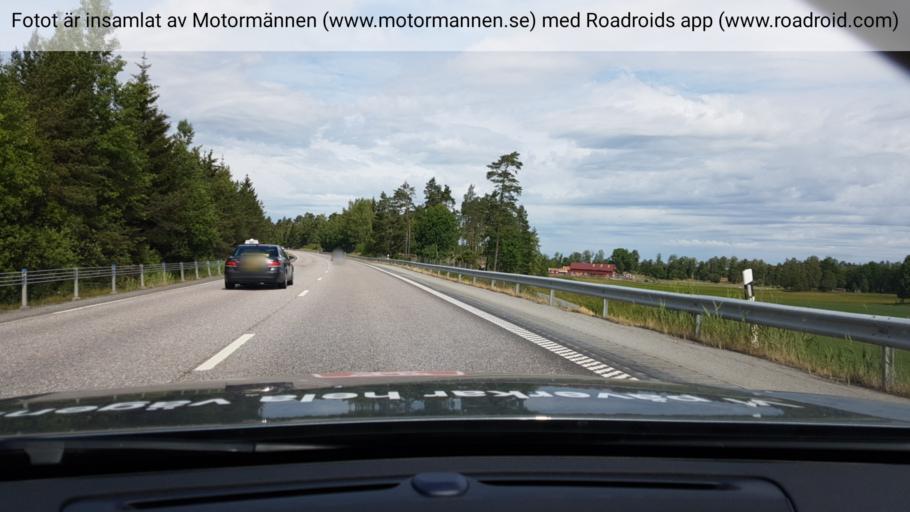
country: SE
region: Uppsala
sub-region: Knivsta Kommun
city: Knivsta
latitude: 59.7159
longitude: 17.8473
